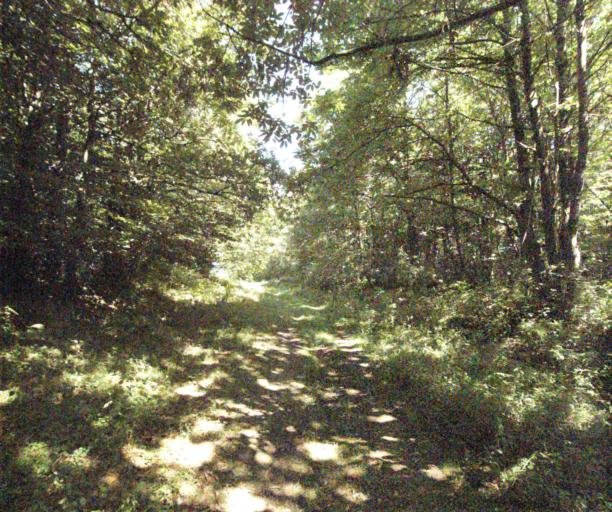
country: FR
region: Midi-Pyrenees
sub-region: Departement du Tarn
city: Soreze
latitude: 43.4390
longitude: 2.1080
